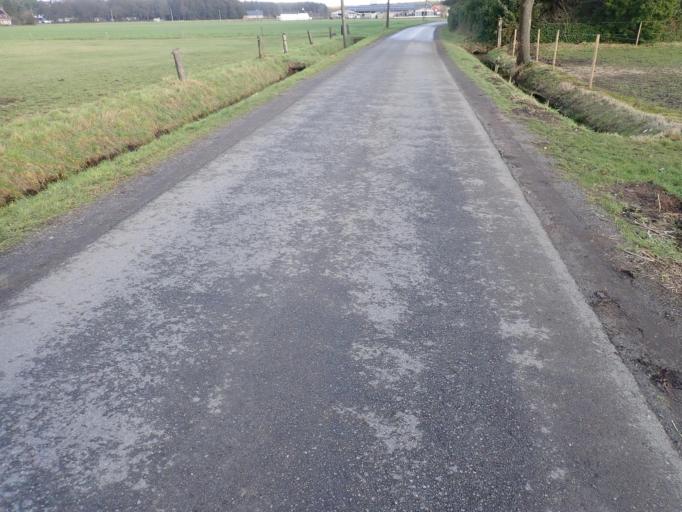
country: BE
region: Flanders
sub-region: Provincie Antwerpen
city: Grobbendonk
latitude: 51.2242
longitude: 4.7118
